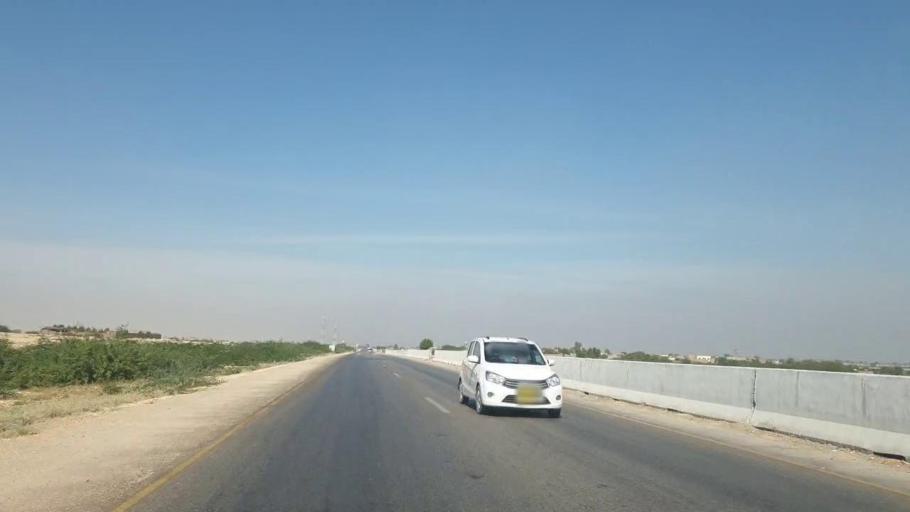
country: PK
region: Sindh
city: Hala
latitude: 25.6931
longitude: 68.2955
